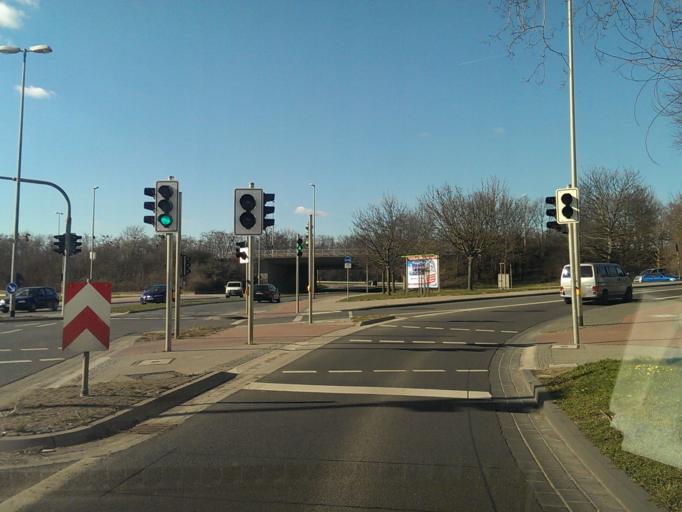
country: DE
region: Lower Saxony
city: Hildesheim
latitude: 52.1525
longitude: 9.9358
